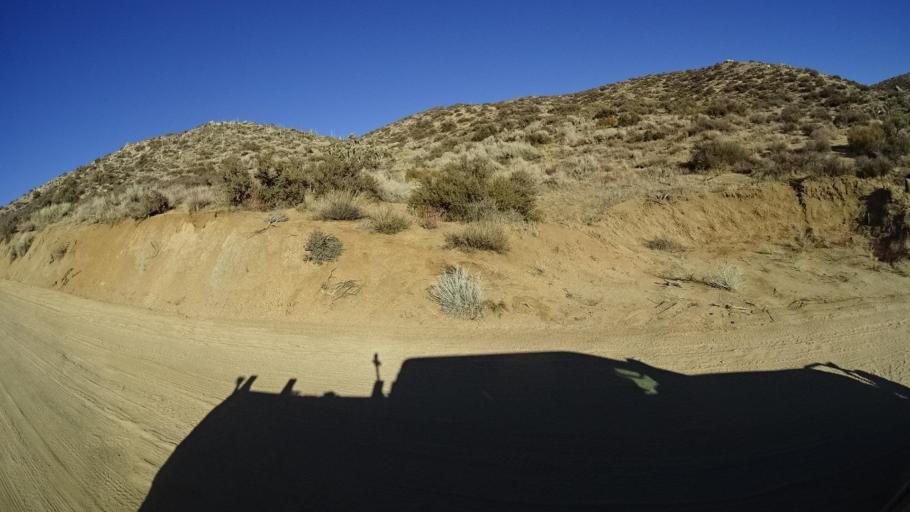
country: US
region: California
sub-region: Kern County
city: Weldon
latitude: 35.4480
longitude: -118.2251
